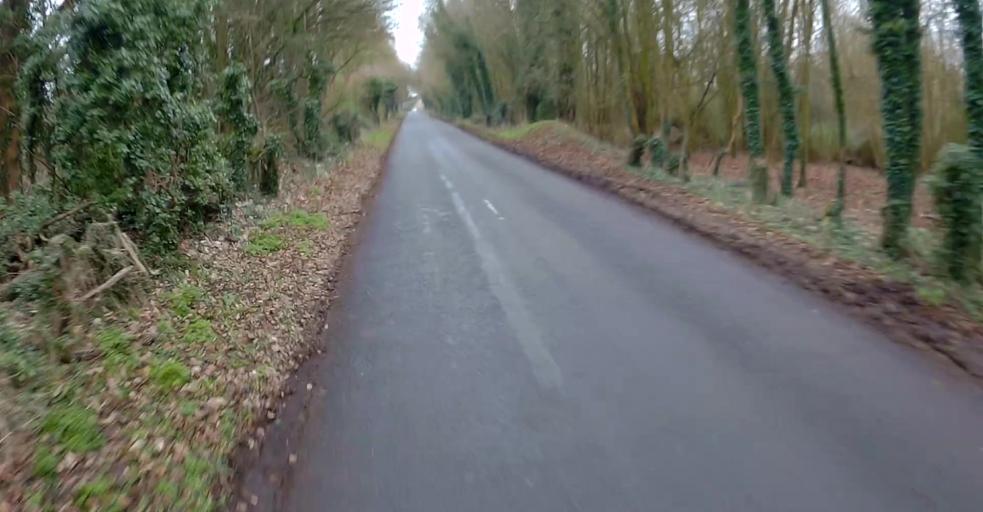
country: GB
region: England
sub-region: Hampshire
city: Old Basing
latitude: 51.2723
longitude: -1.0584
